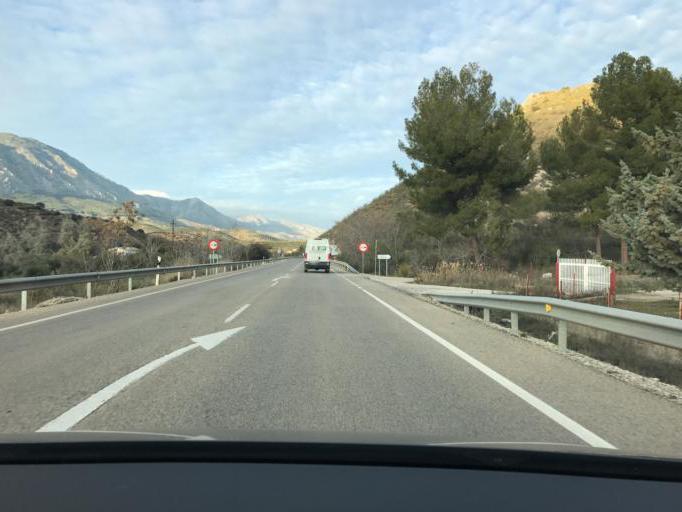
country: ES
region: Andalusia
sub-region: Provincia de Jaen
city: Huelma
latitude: 37.6594
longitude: -3.4183
